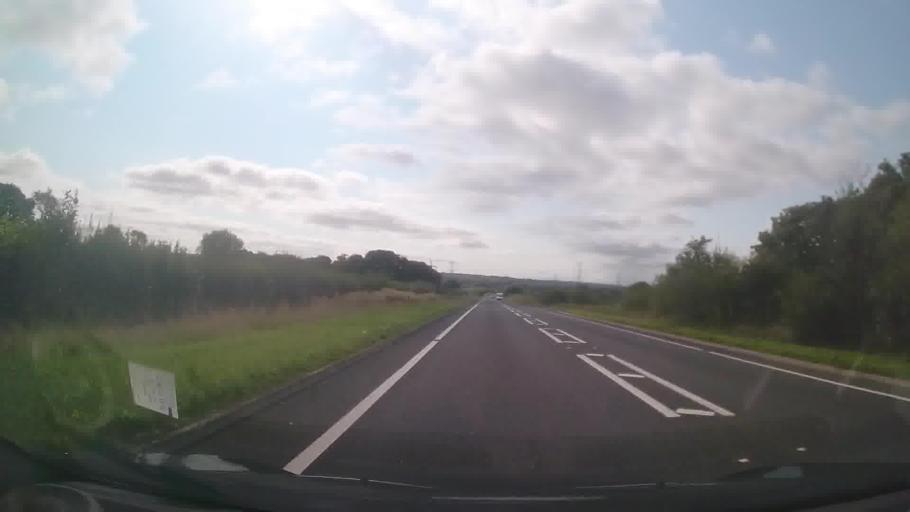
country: GB
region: Wales
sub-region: Pembrokeshire
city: Jeffreyston
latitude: 51.6999
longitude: -4.7799
